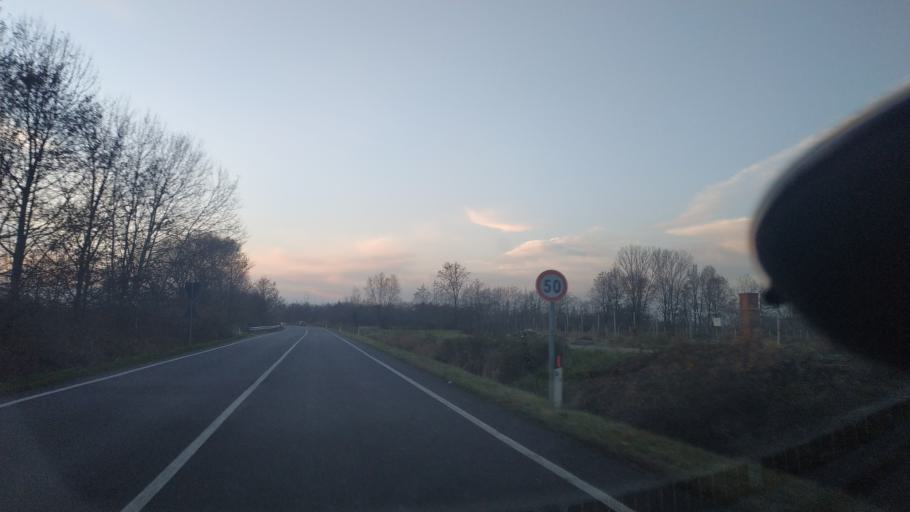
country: IT
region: Piedmont
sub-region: Provincia di Torino
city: Montanaro
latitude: 45.2429
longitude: 7.8556
